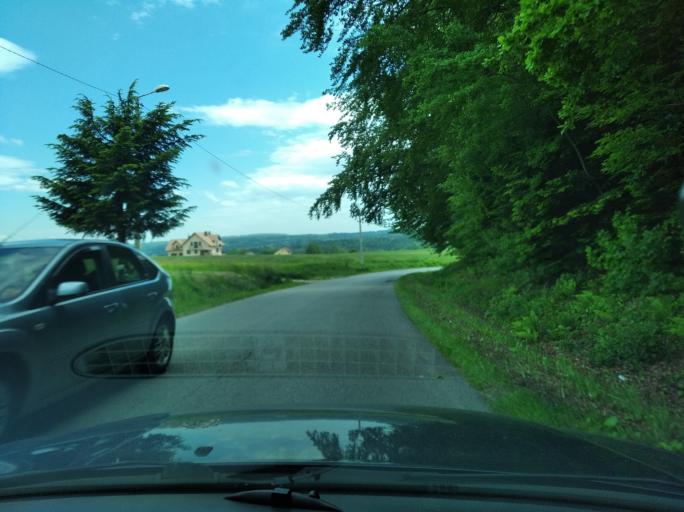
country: PL
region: Subcarpathian Voivodeship
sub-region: Powiat ropczycko-sedziszowski
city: Ropczyce
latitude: 50.0074
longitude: 21.6135
